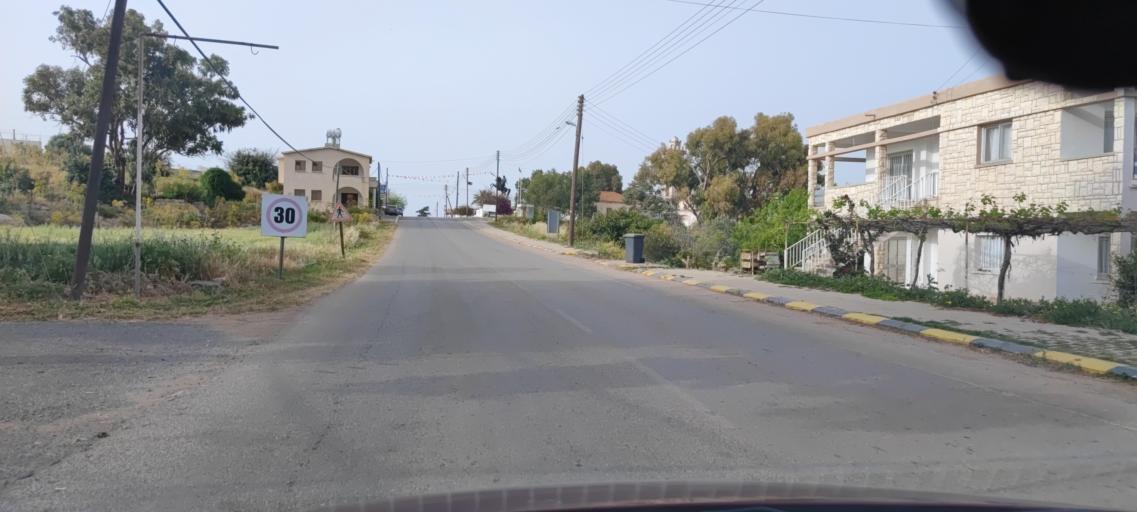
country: CY
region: Ammochostos
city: Leonarisso
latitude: 35.5016
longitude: 34.1610
